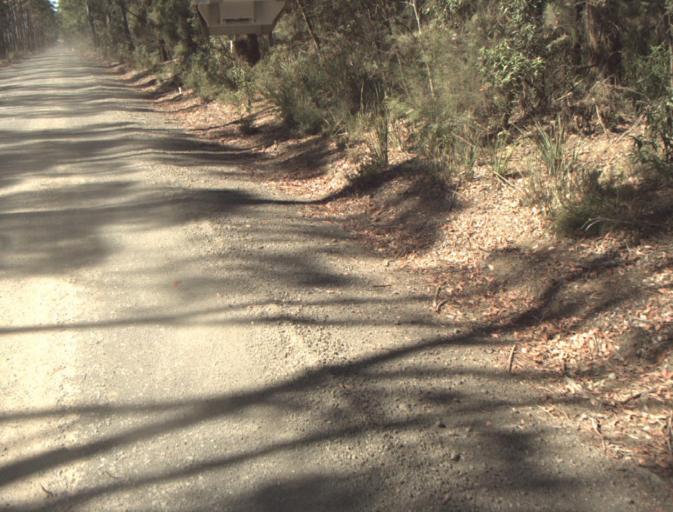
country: AU
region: Tasmania
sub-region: Launceston
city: Newstead
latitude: -41.3552
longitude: 147.2233
